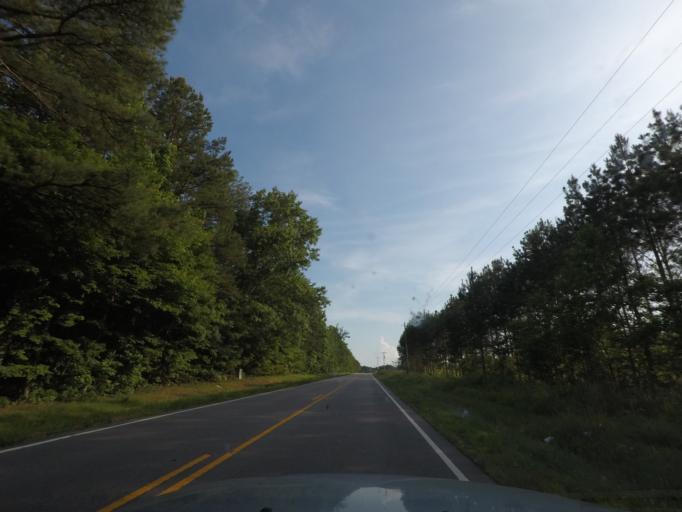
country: US
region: North Carolina
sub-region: Granville County
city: Oxford
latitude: 36.4200
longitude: -78.5864
